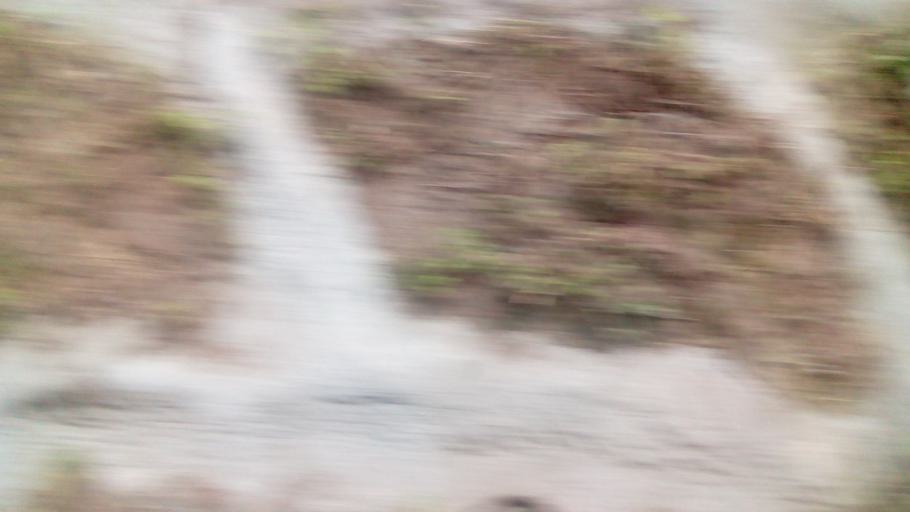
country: TW
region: Taiwan
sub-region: Yilan
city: Yilan
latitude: 24.5614
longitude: 121.4770
